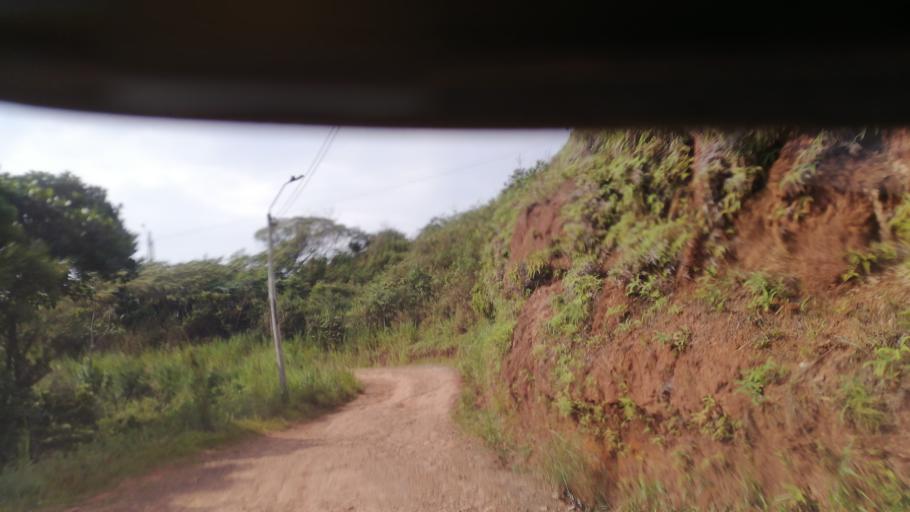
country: CO
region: Valle del Cauca
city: Cali
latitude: 3.4949
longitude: -76.5434
